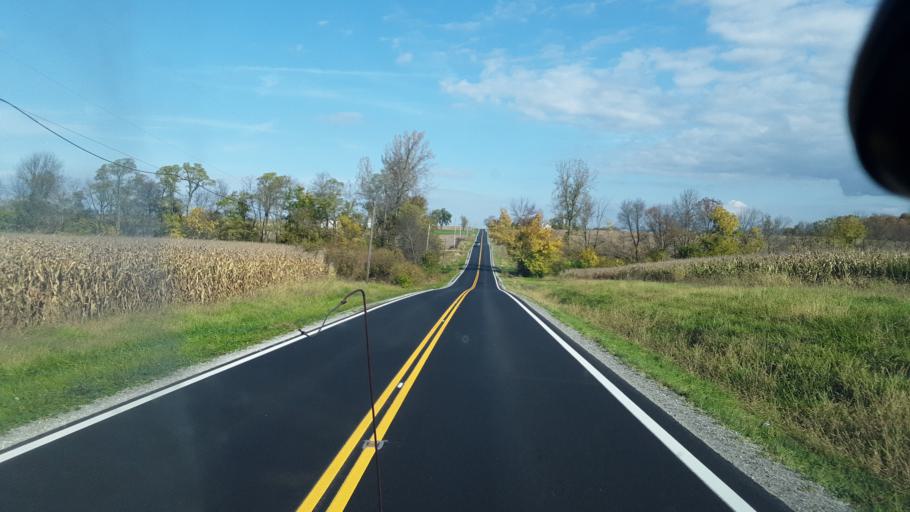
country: US
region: Ohio
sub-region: Highland County
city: Leesburg
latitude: 39.3031
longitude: -83.5889
